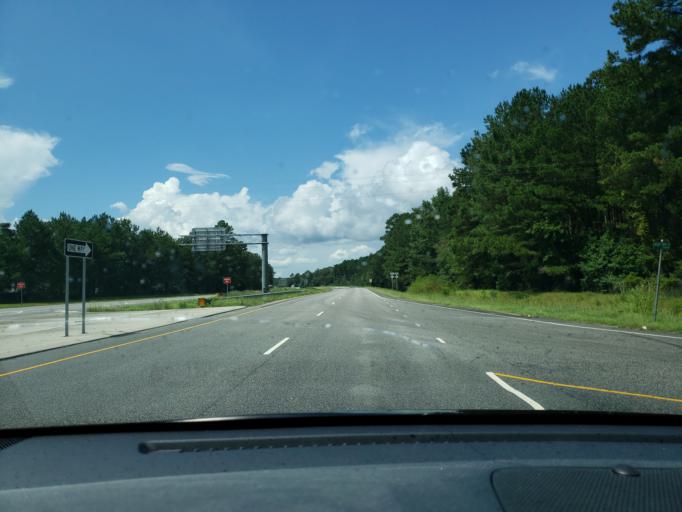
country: US
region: North Carolina
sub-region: Bladen County
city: Elizabethtown
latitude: 34.6420
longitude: -78.6757
